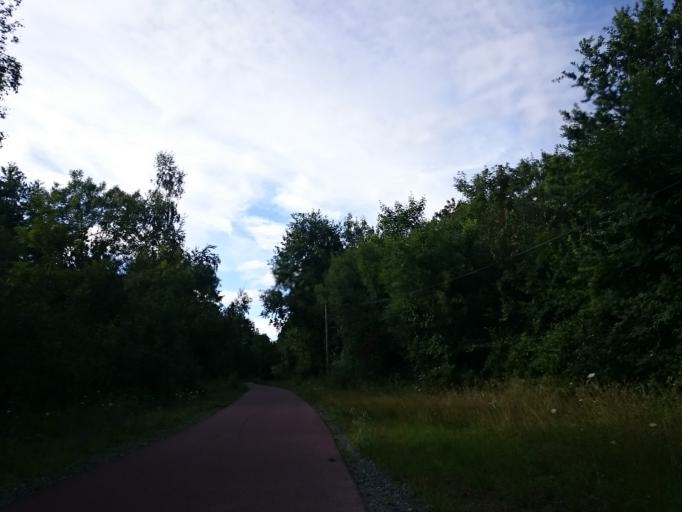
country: FR
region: Lower Normandy
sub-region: Departement du Calvados
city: Saint-Andre-sur-Orne
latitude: 49.1086
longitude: -0.3857
